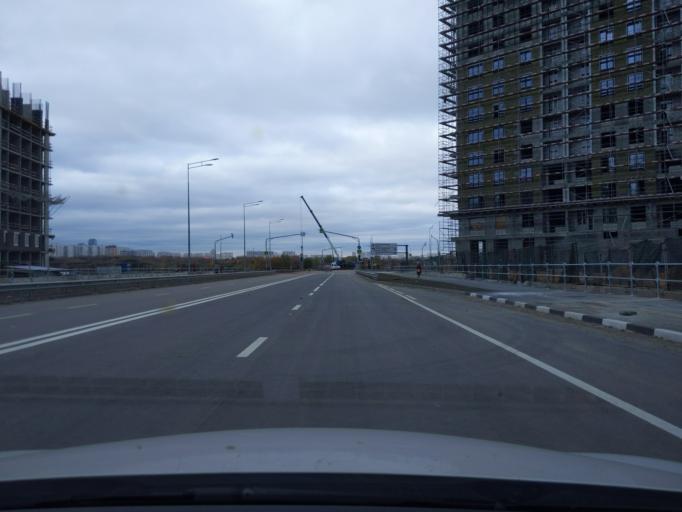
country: RU
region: Moscow
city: Strogino
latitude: 55.8163
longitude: 37.4273
